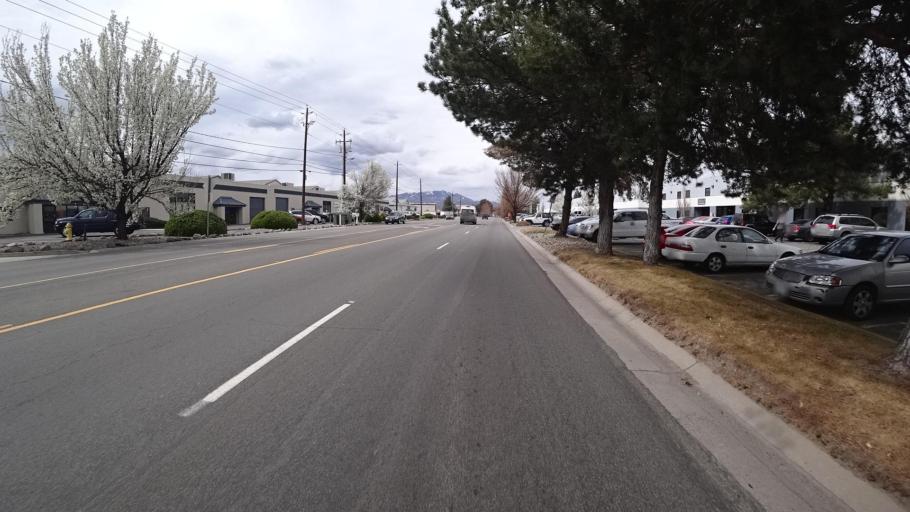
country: US
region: Nevada
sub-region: Washoe County
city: Sparks
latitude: 39.5218
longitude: -119.7549
